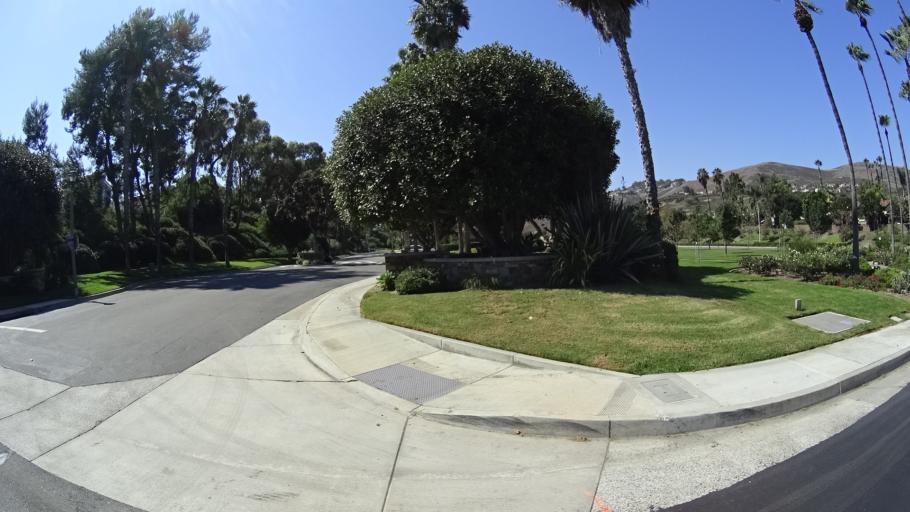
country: US
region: California
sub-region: Orange County
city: San Juan Capistrano
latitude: 33.4687
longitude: -117.6332
